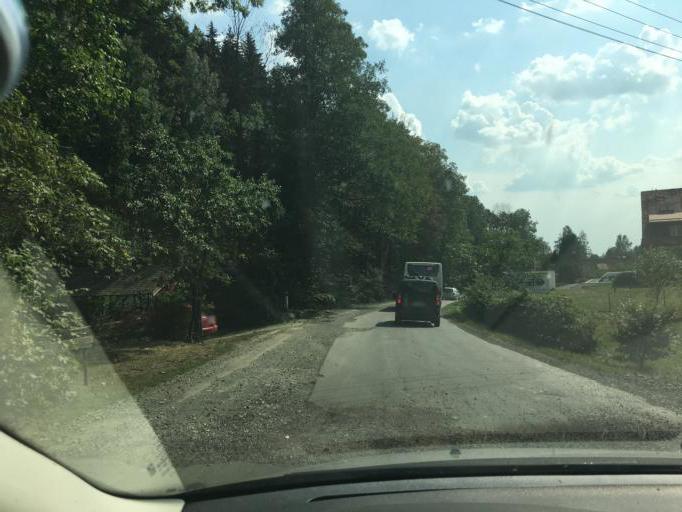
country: CZ
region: Kralovehradecky
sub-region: Okres Trutnov
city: Rudnik
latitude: 50.6258
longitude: 15.7134
